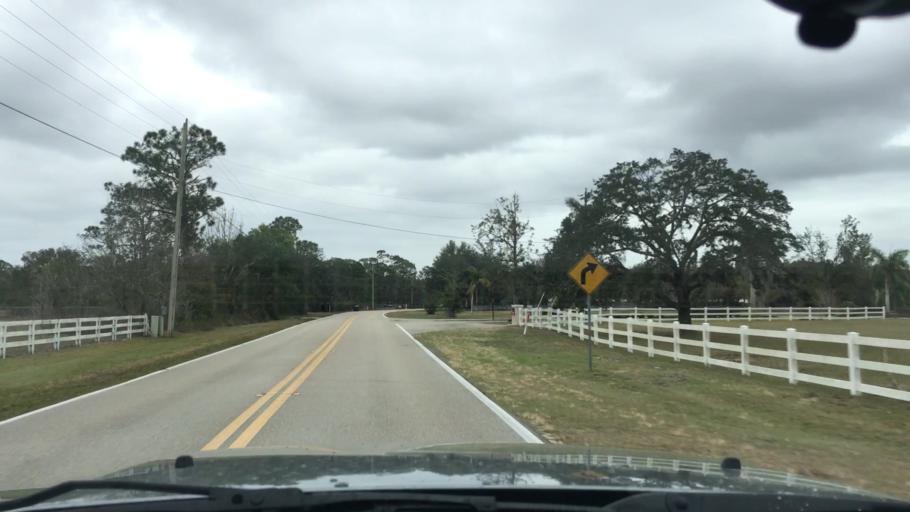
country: US
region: Florida
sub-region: Highlands County
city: Sebring
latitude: 27.4404
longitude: -81.4486
